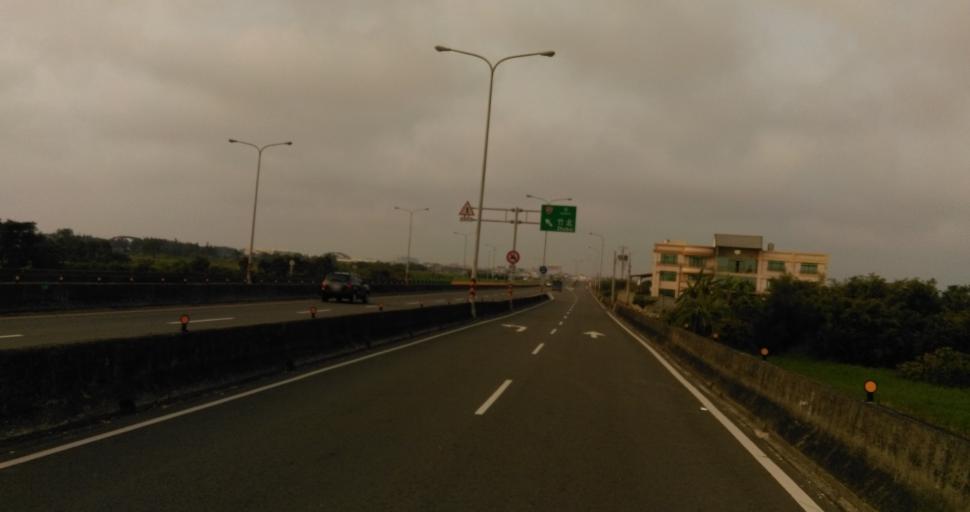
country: TW
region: Taiwan
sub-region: Hsinchu
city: Hsinchu
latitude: 24.7945
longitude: 120.9197
